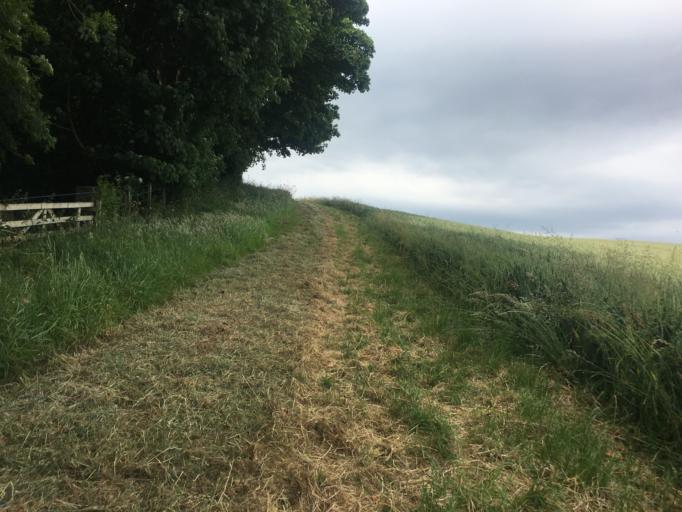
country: GB
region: England
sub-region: Northumberland
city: Bamburgh
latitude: 55.6021
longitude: -1.7727
